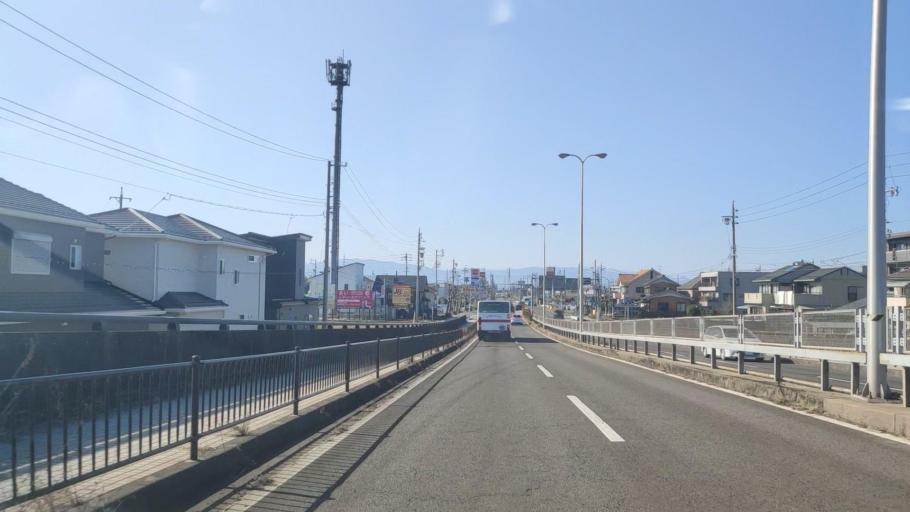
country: JP
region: Gifu
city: Gifu-shi
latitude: 35.4241
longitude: 136.7386
